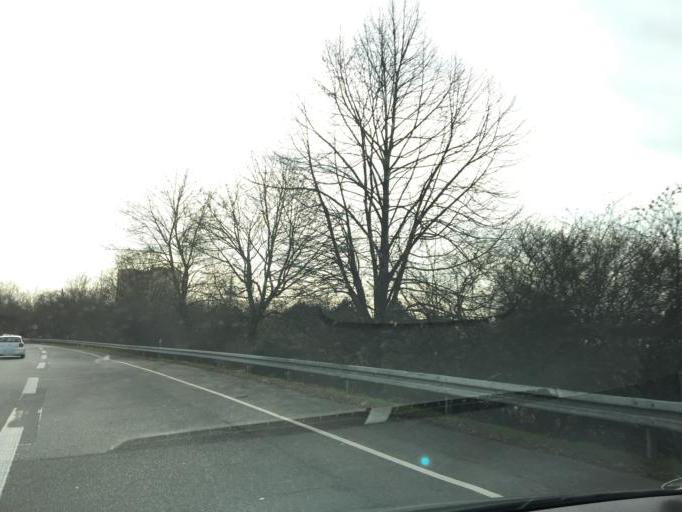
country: DE
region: Hesse
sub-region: Regierungsbezirk Darmstadt
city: Frankfurt am Main
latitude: 50.1552
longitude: 8.6752
